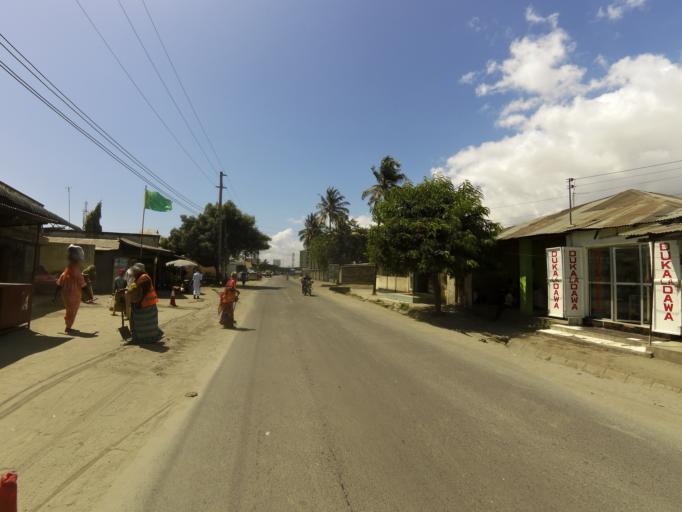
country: TZ
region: Dar es Salaam
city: Magomeni
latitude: -6.8031
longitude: 39.2589
